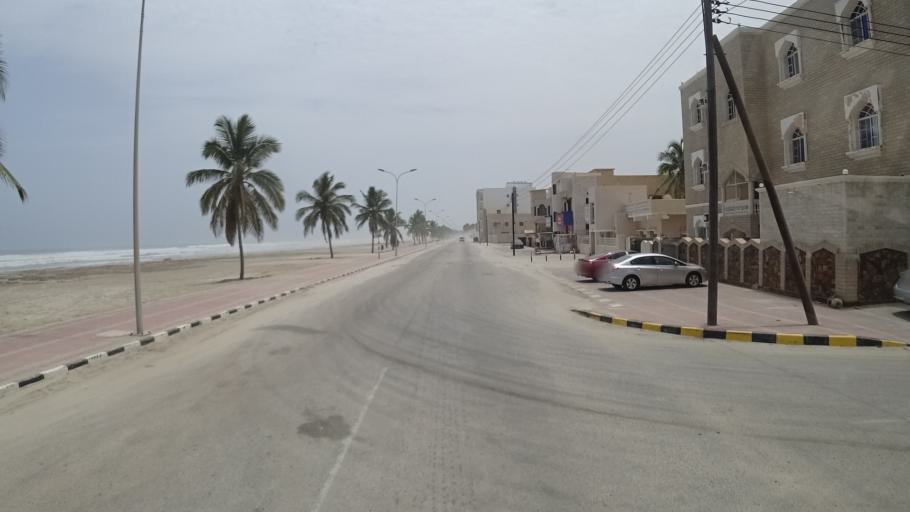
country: OM
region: Zufar
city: Salalah
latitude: 17.0343
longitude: 54.3988
